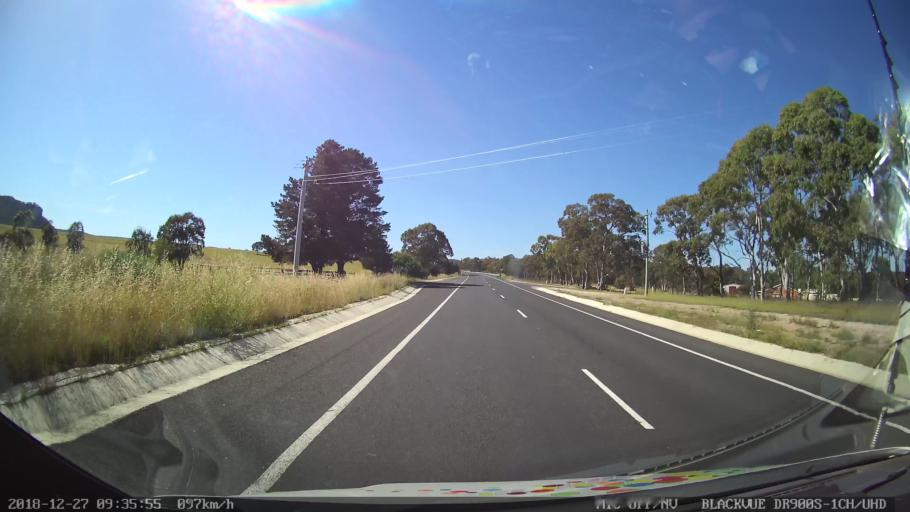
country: AU
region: New South Wales
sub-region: Lithgow
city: Portland
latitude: -33.2451
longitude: 150.0327
